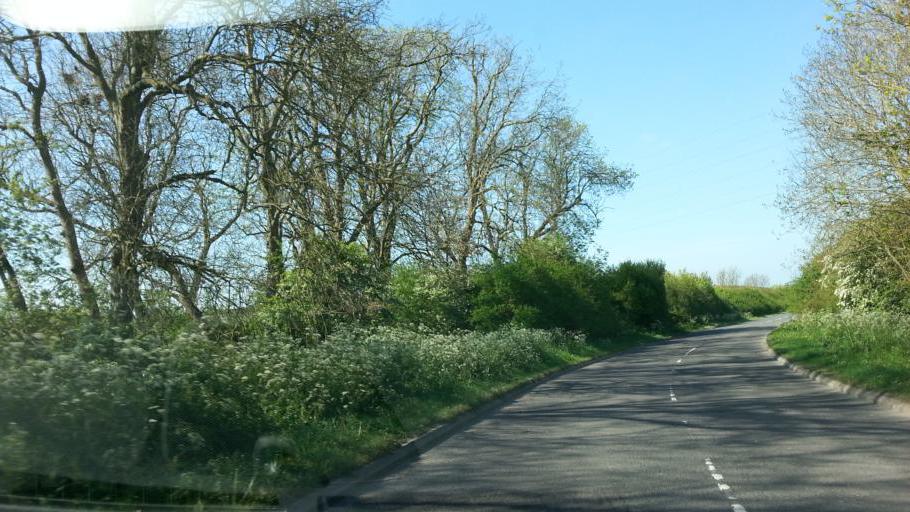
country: GB
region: England
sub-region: Nottinghamshire
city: Newark on Trent
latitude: 53.0192
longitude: -0.8039
